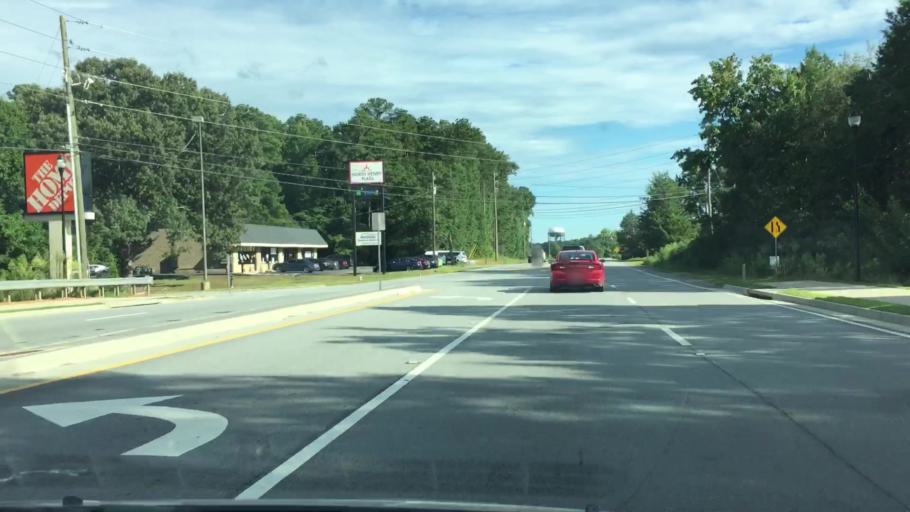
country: US
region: Georgia
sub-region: Henry County
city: Stockbridge
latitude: 33.6197
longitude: -84.2352
